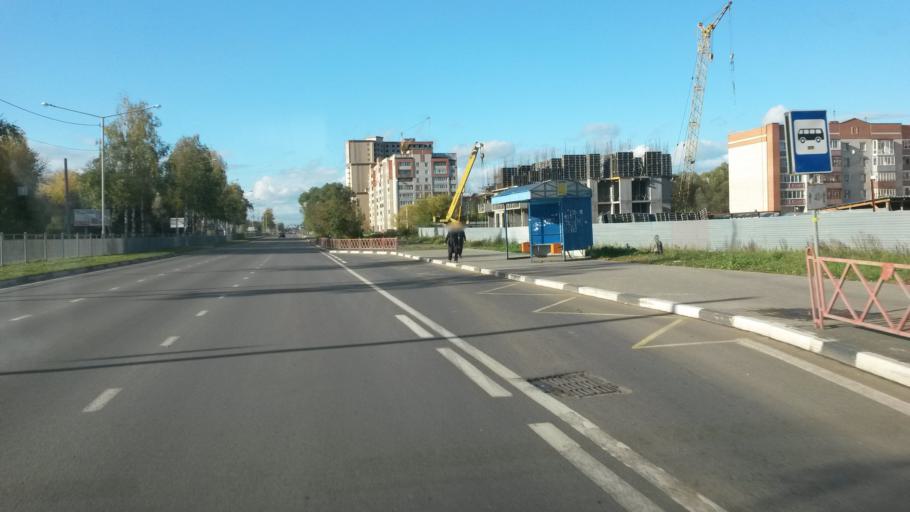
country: RU
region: Jaroslavl
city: Yaroslavl
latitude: 57.5616
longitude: 39.9349
